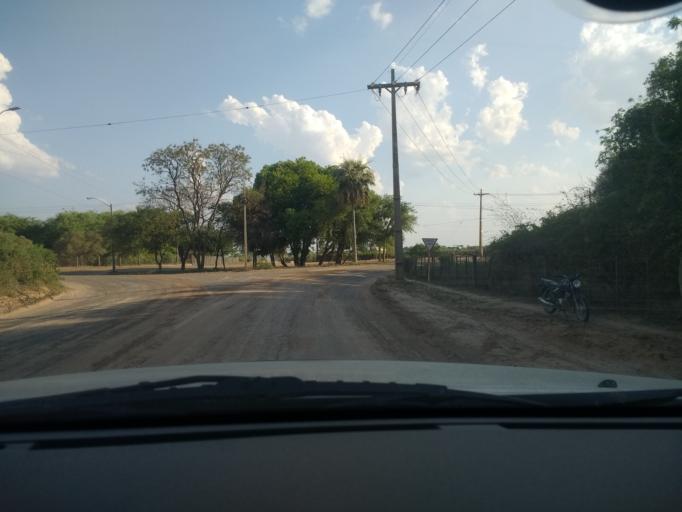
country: PY
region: Boqueron
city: Colonia Menno
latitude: -22.3882
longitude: -59.8140
